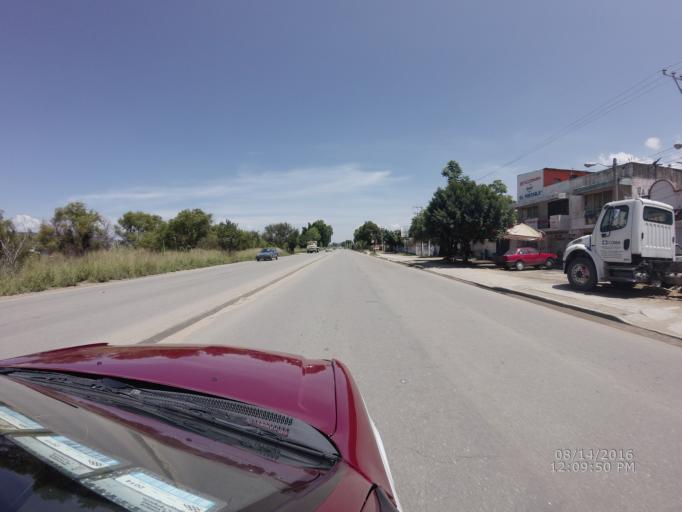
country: MX
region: Oaxaca
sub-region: Santa Maria Atzompa
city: La Canada
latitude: 17.0840
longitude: -96.7497
